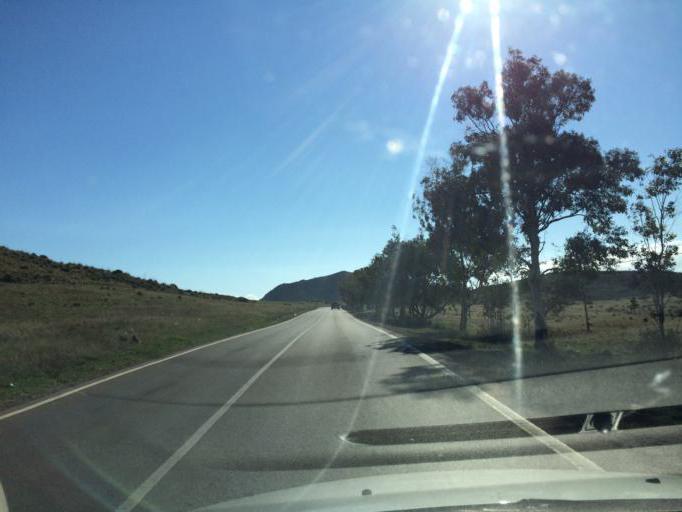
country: ES
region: Andalusia
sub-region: Provincia de Almeria
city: San Jose
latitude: 36.7856
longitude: -2.1086
